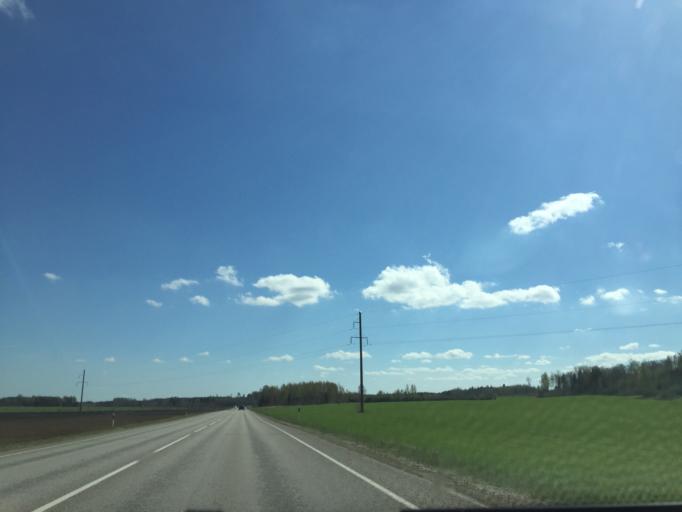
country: EE
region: Valgamaa
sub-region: Valga linn
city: Valga
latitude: 57.8814
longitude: 26.0594
